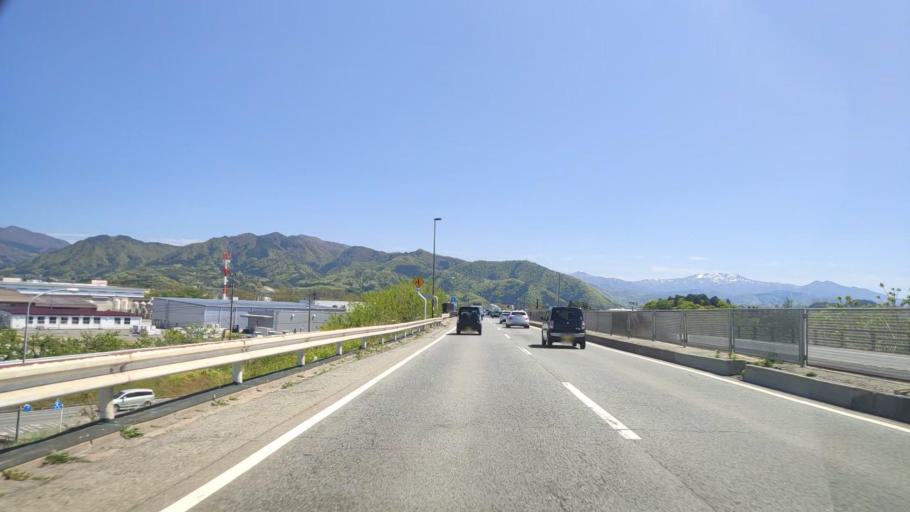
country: JP
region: Yamagata
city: Tendo
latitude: 38.3963
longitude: 140.3768
